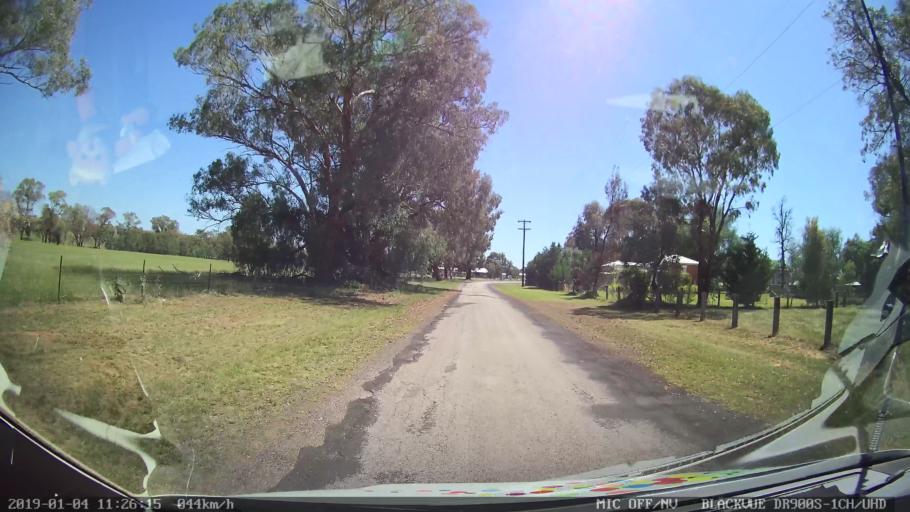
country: AU
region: New South Wales
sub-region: Cabonne
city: Molong
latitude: -33.1165
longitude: 148.7555
